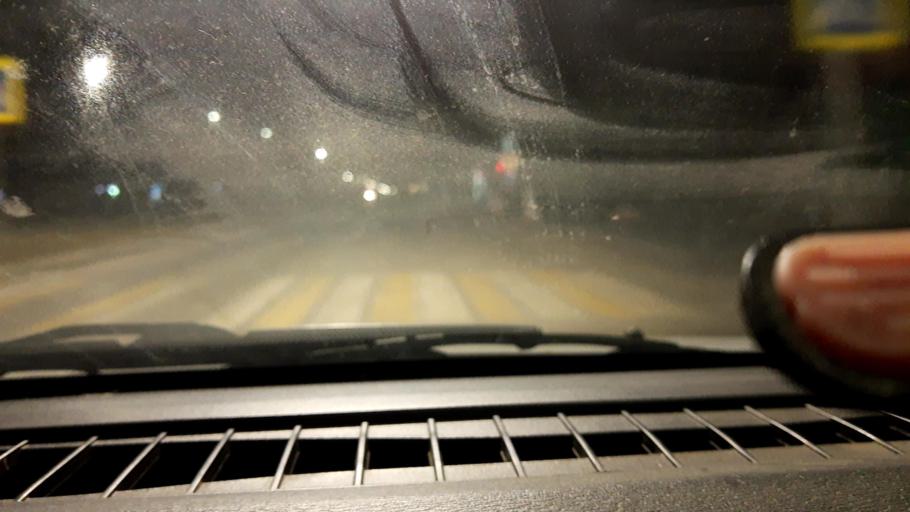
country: RU
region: Nizjnij Novgorod
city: Dzerzhinsk
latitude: 56.2378
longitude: 43.4583
